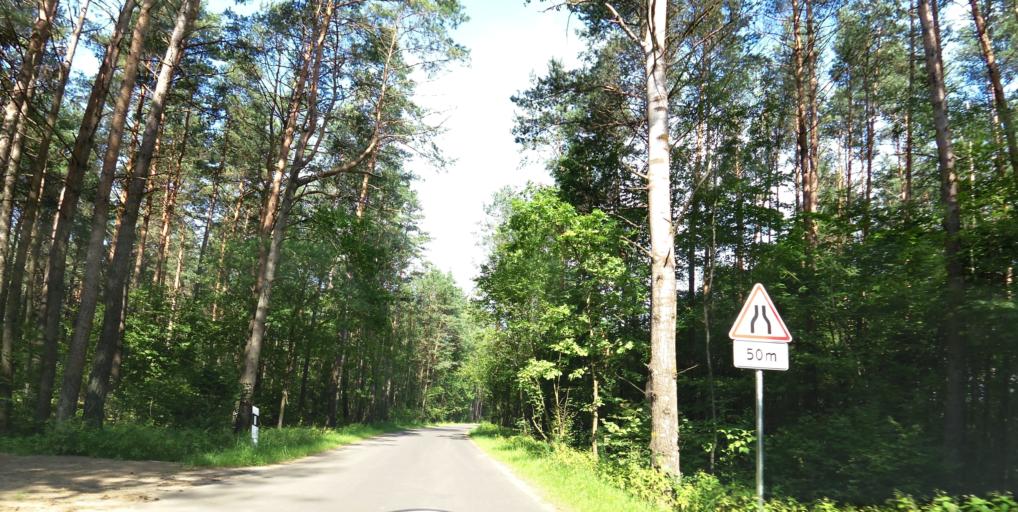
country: LT
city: Grigiskes
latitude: 54.7255
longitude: 25.0491
